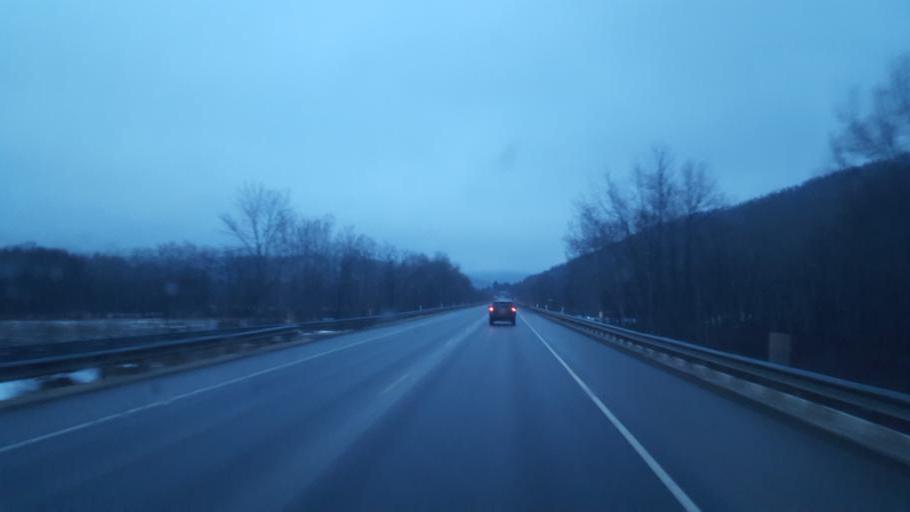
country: US
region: Pennsylvania
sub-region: McKean County
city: Port Allegany
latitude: 41.7990
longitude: -78.2603
